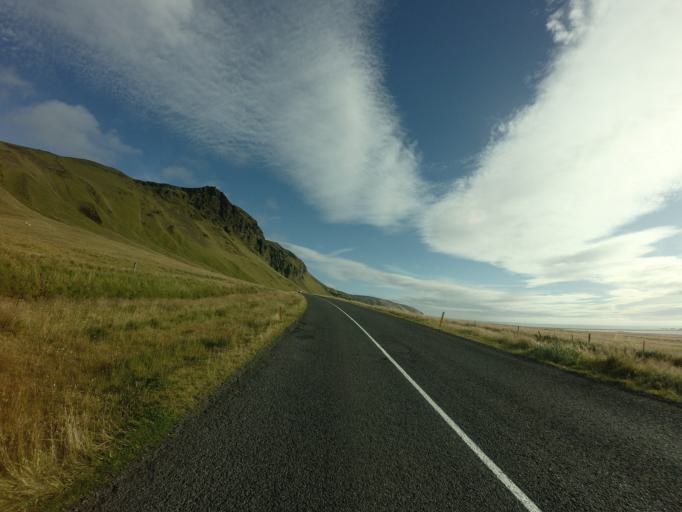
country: IS
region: South
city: Vestmannaeyjar
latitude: 63.4366
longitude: -19.0590
